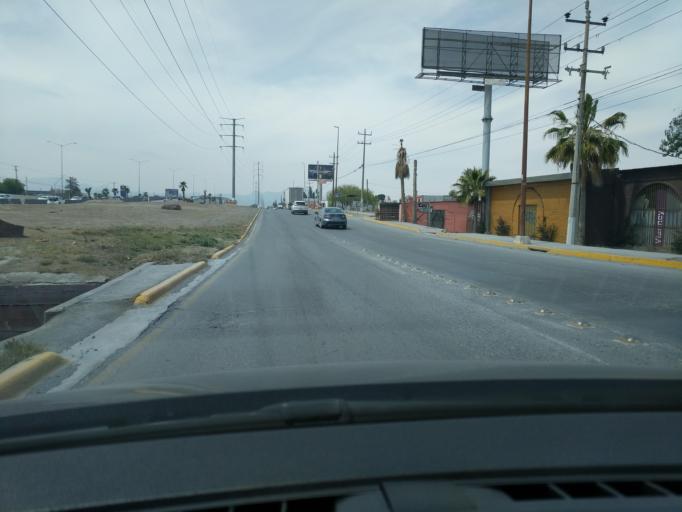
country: MX
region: Coahuila
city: Saltillo
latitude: 25.4314
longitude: -100.9432
